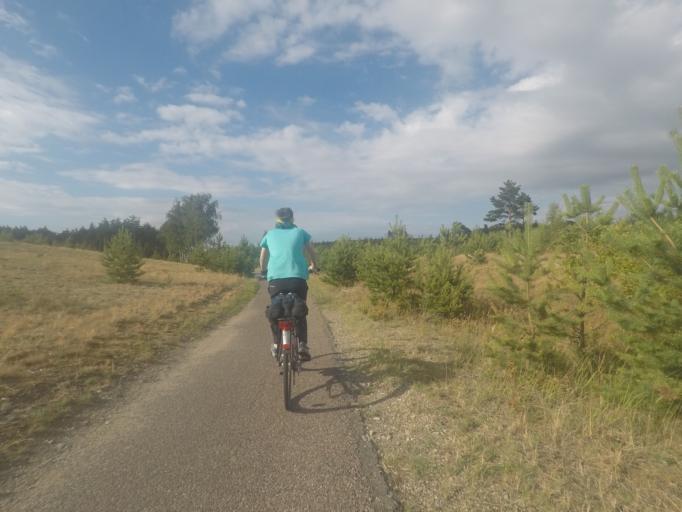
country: LT
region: Klaipedos apskritis
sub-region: Klaipeda
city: Klaipeda
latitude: 55.6352
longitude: 21.1170
